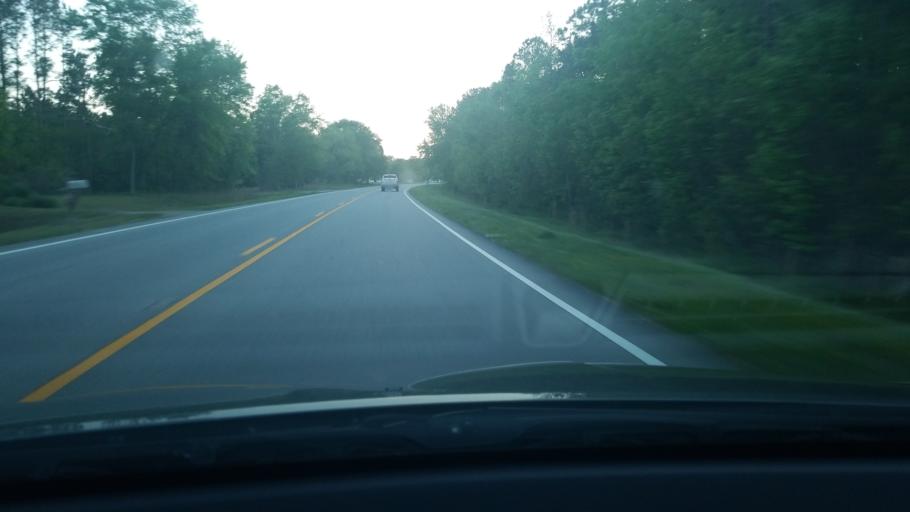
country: US
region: North Carolina
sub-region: Craven County
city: Vanceboro
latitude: 35.2350
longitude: -77.1052
